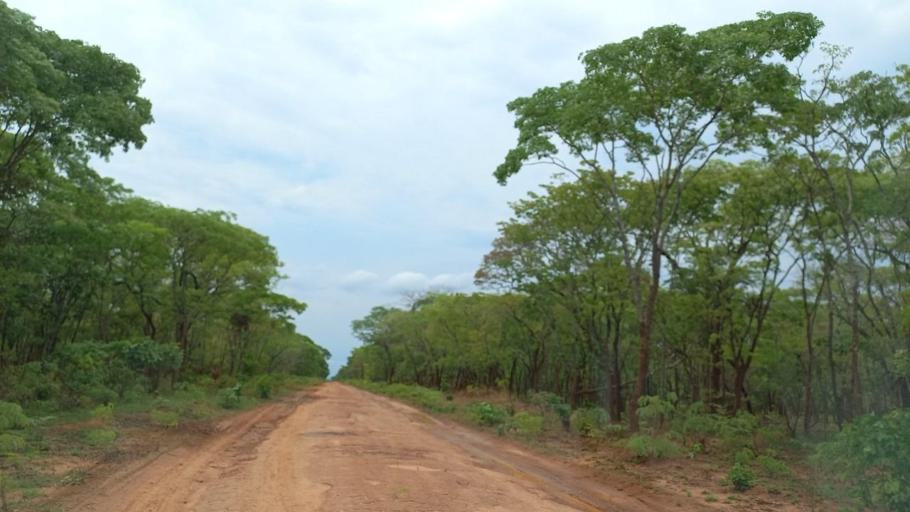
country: ZM
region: North-Western
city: Kalengwa
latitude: -13.6094
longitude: 24.9753
